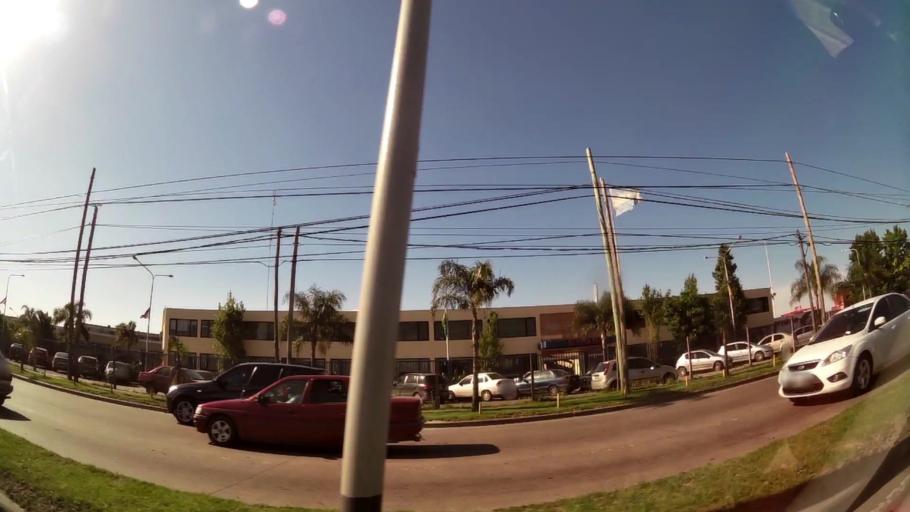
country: AR
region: Buenos Aires
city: Santa Catalina - Dique Lujan
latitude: -34.4779
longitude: -58.6677
